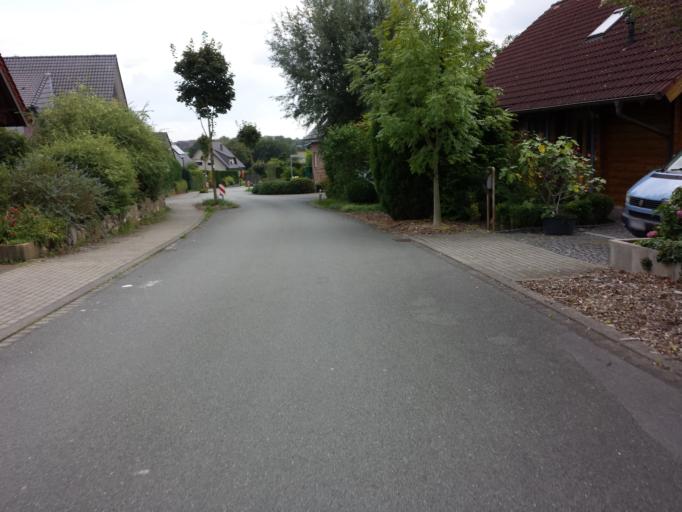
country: DE
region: North Rhine-Westphalia
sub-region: Regierungsbezirk Detmold
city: Langenberg
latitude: 51.7832
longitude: 8.3081
